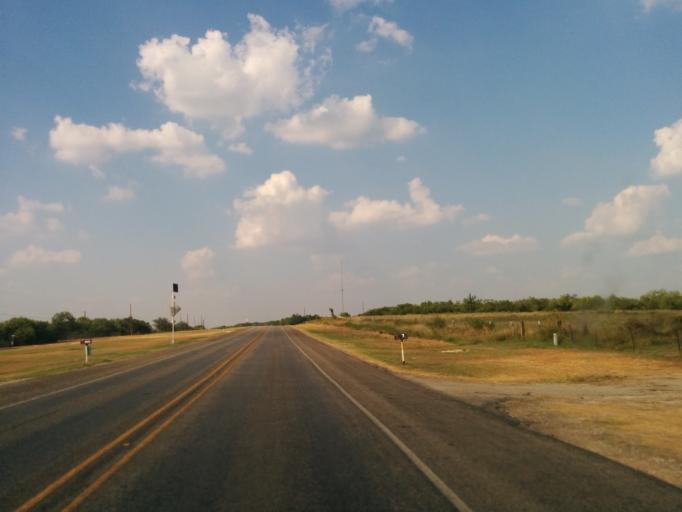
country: US
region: Texas
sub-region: Bexar County
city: Saint Hedwig
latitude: 29.3301
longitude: -98.2574
